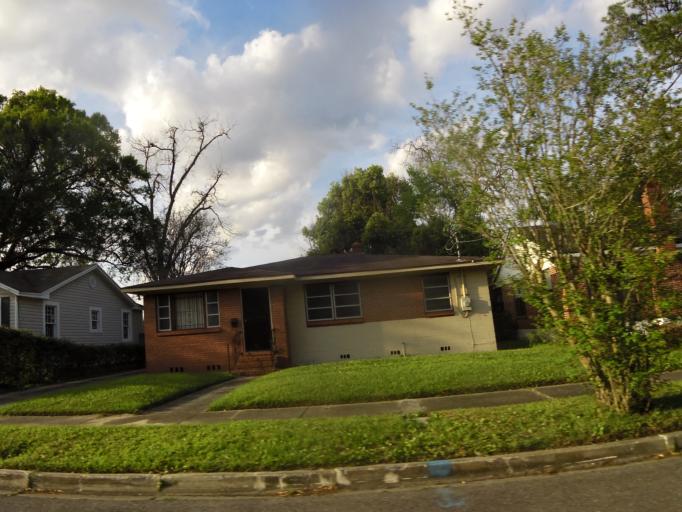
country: US
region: Florida
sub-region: Duval County
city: Jacksonville
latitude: 30.3490
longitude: -81.6790
